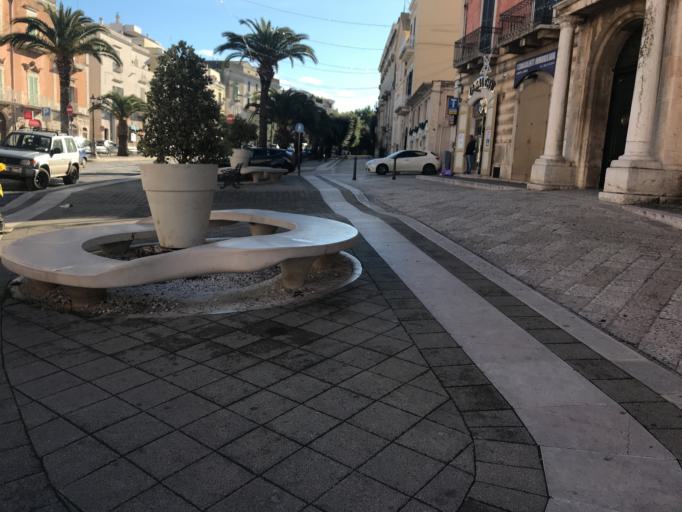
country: IT
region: Apulia
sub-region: Provincia di Bari
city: Corato
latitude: 41.1536
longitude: 16.4131
